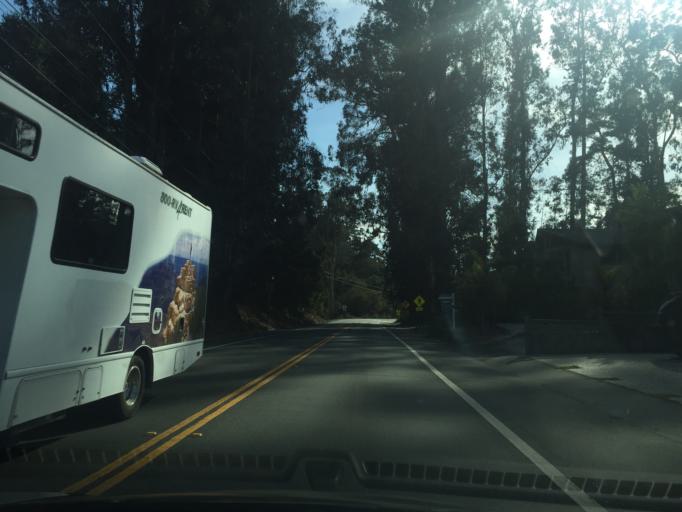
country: US
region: California
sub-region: Santa Cruz County
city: La Selva Beach
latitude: 36.9387
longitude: -121.8581
